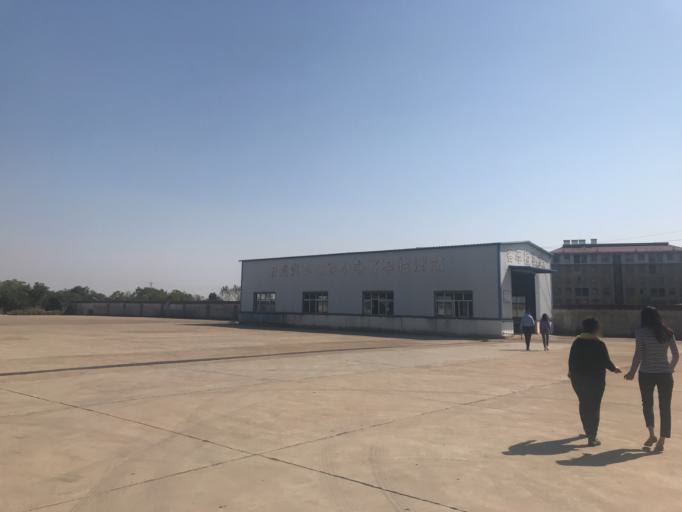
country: CN
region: Hubei
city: Anlu
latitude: 31.2401
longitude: 113.6889
